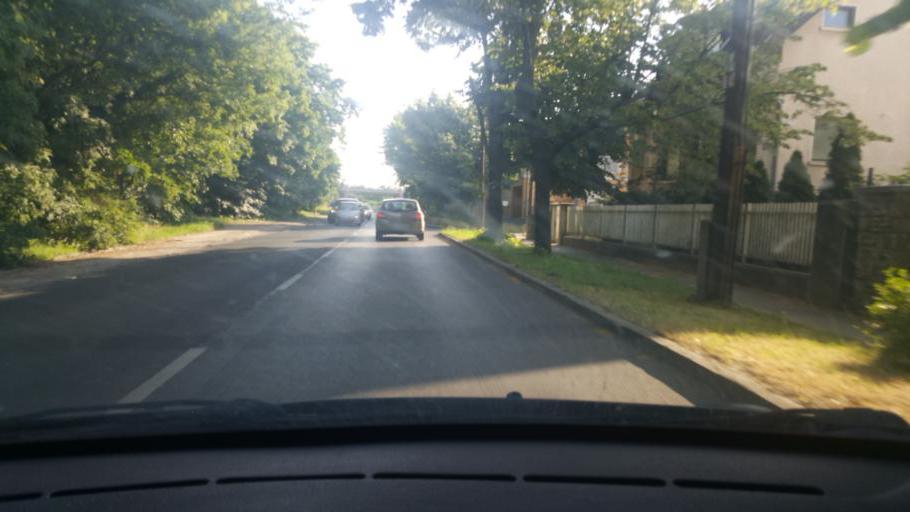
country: HU
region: Budapest
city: Budapest XVIII. keruelet
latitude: 47.4544
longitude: 19.1981
